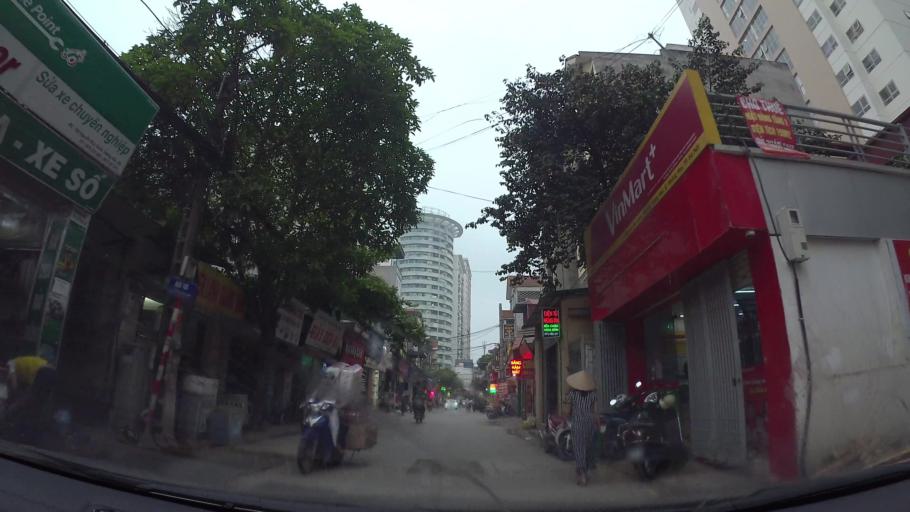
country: VN
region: Ha Noi
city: Hai BaTrung
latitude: 20.9872
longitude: 105.8500
